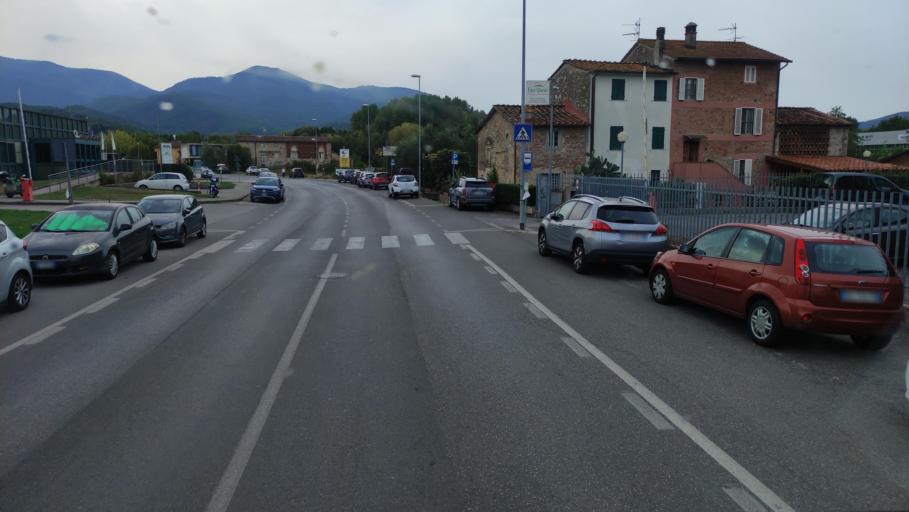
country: IT
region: Tuscany
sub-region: Provincia di Lucca
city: Lucca
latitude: 43.8146
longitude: 10.4975
